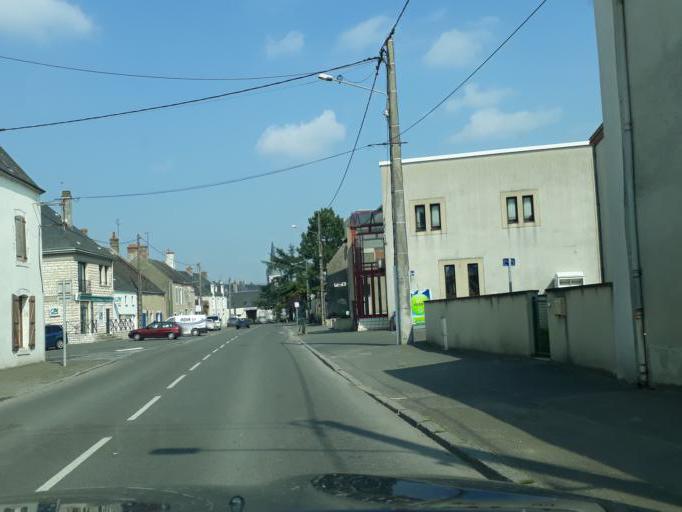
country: FR
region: Centre
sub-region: Departement du Loiret
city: Artenay
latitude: 48.0799
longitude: 1.8787
